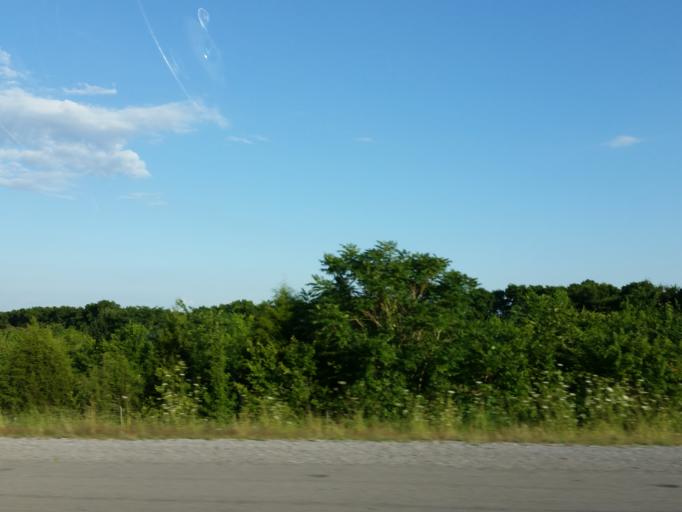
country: US
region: Tennessee
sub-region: Rutherford County
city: Murfreesboro
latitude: 35.8719
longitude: -86.4989
